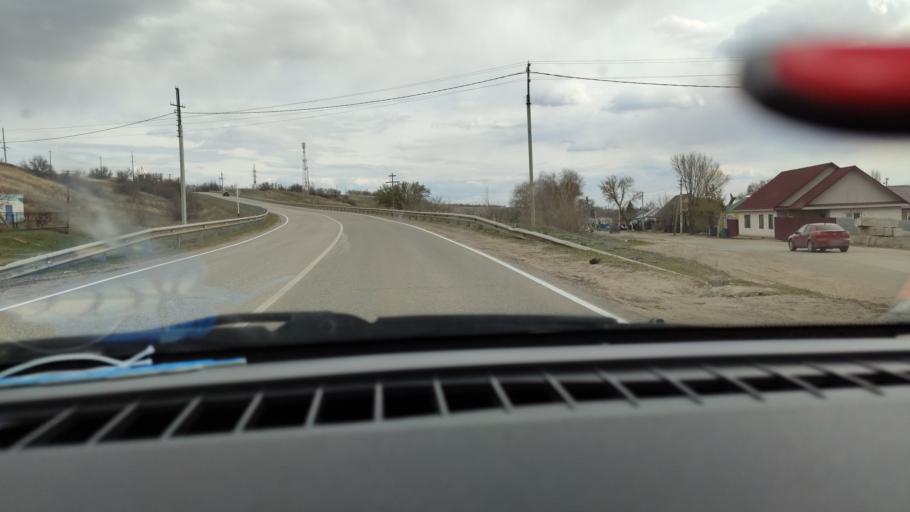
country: RU
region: Saratov
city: Privolzhskiy
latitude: 51.1790
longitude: 45.9237
